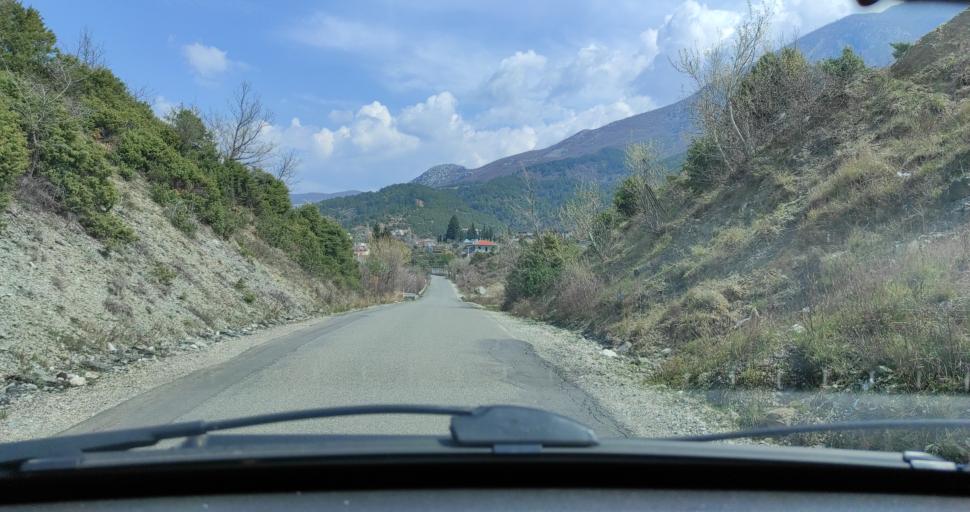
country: AL
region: Lezhe
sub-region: Rrethi i Lezhes
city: Kallmeti i Madh
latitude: 41.8466
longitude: 19.6858
